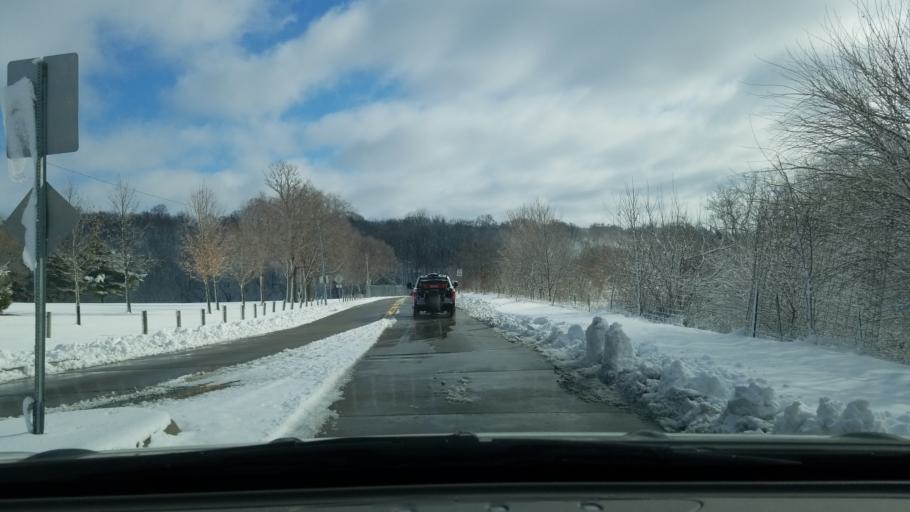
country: US
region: Nebraska
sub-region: Douglas County
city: Omaha
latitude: 41.2200
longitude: -95.9382
